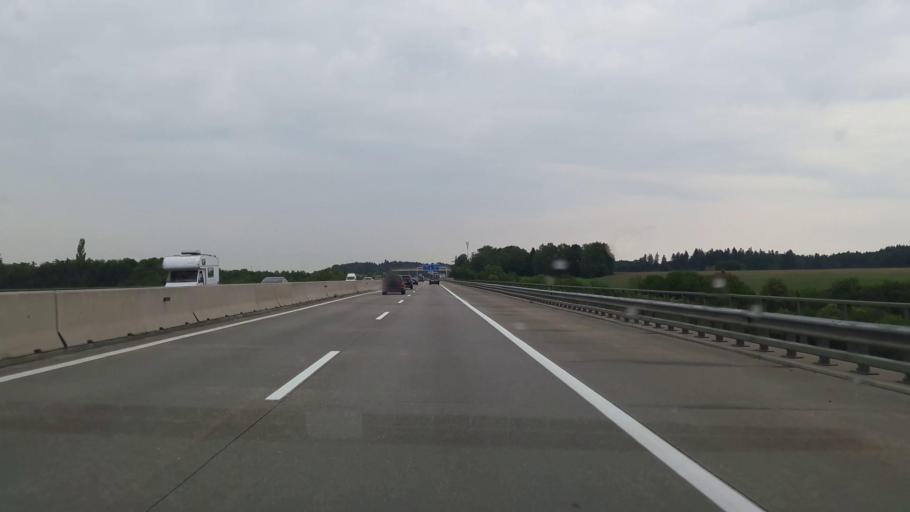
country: AT
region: Upper Austria
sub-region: Wels-Land
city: Sattledt
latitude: 48.0502
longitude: 14.0170
